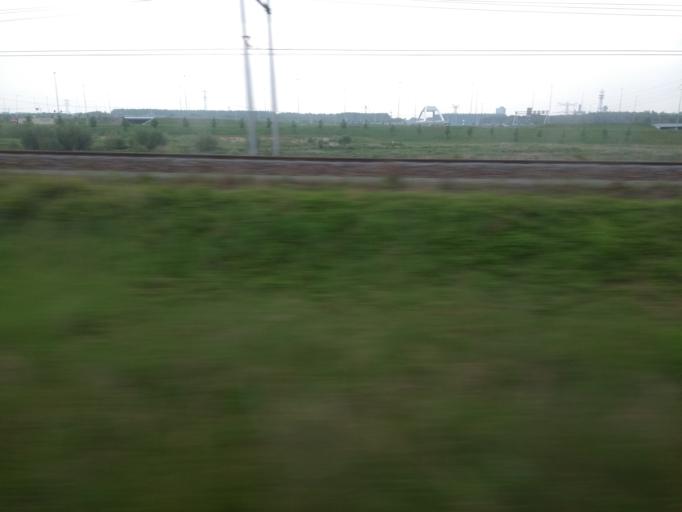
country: NL
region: North Holland
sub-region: Gemeente Amsterdam
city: Driemond
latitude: 52.3313
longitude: 4.9999
